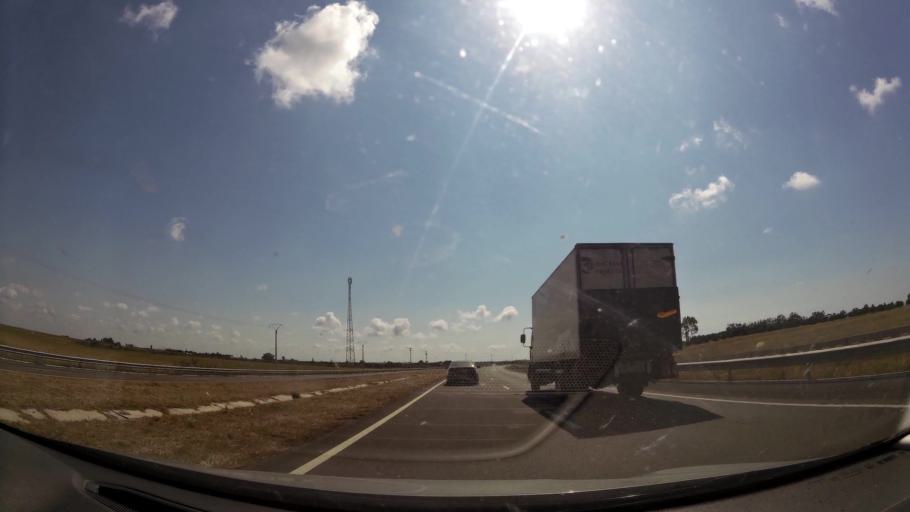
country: MA
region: Rabat-Sale-Zemmour-Zaer
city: Skhirat
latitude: 33.8611
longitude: -6.9708
